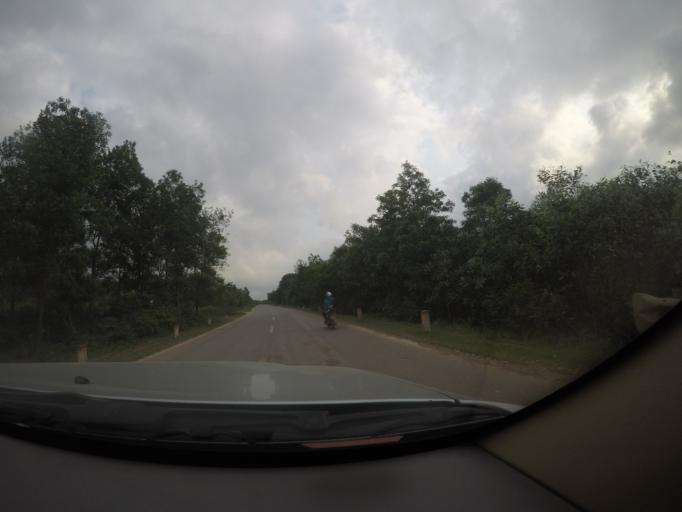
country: VN
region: Quang Tri
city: Ho Xa
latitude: 17.0689
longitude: 106.8599
